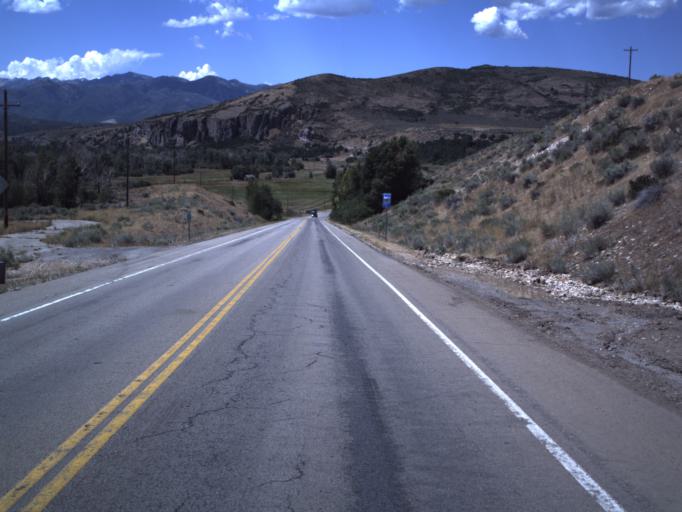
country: US
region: Utah
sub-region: Summit County
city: Francis
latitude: 40.6107
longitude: -111.2875
